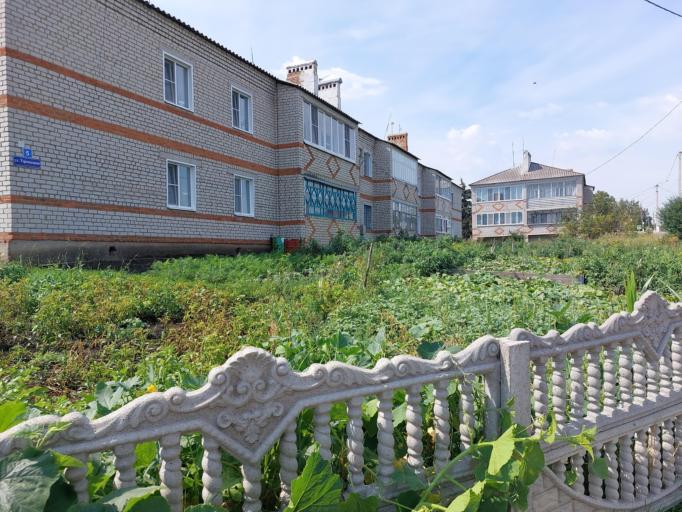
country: RU
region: Lipetsk
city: Dolgorukovo
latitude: 52.3260
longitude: 38.3639
